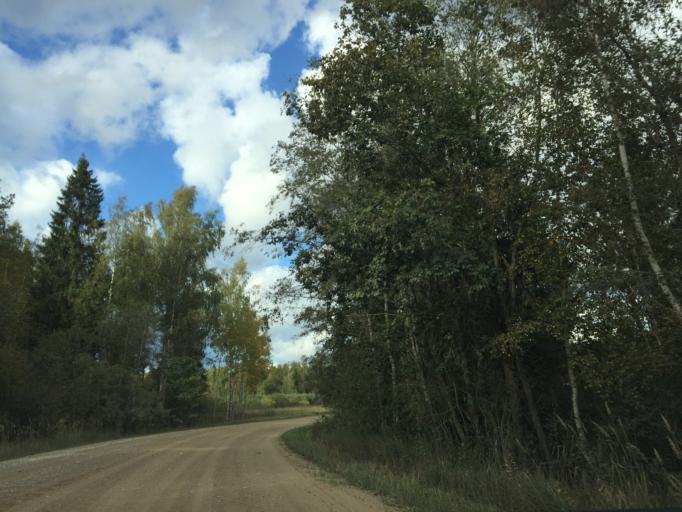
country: LV
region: Malpils
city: Malpils
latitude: 57.0244
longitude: 25.0506
